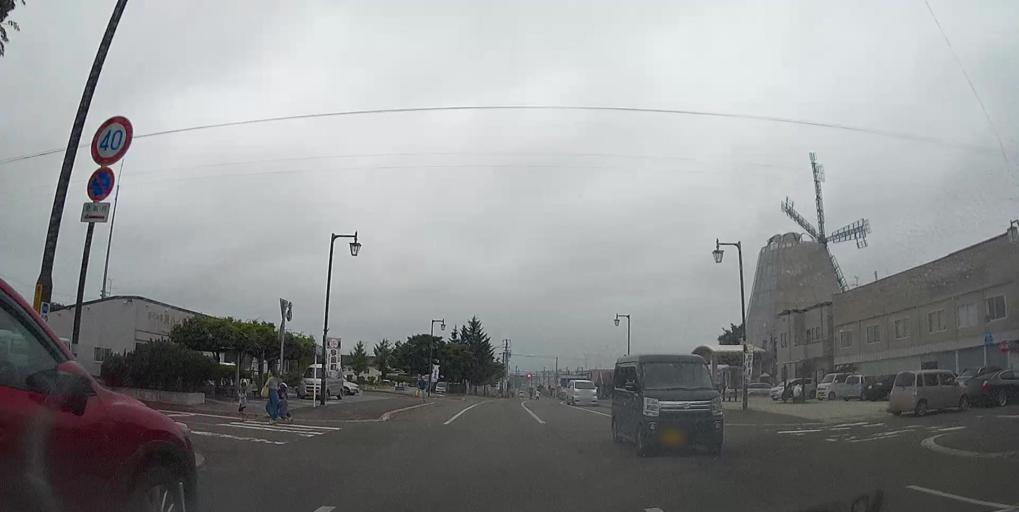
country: JP
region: Hokkaido
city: Iwanai
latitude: 42.4283
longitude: 140.0139
